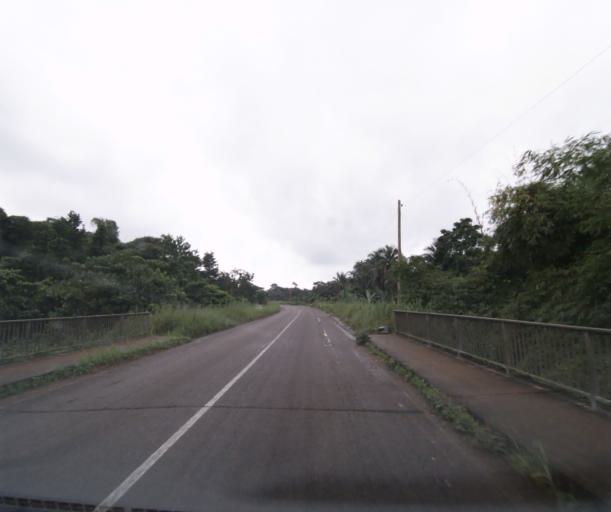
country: CM
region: Littoral
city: Dizangue
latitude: 3.5001
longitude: 10.1179
